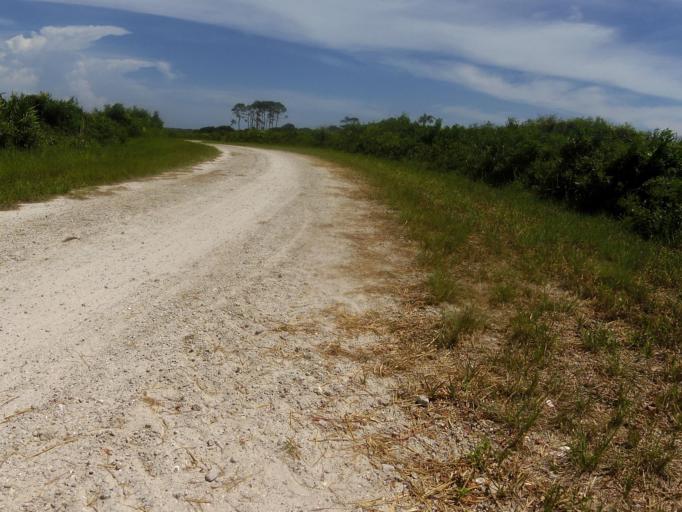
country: US
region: Florida
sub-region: Saint Johns County
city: Villano Beach
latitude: 30.0375
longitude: -81.3367
